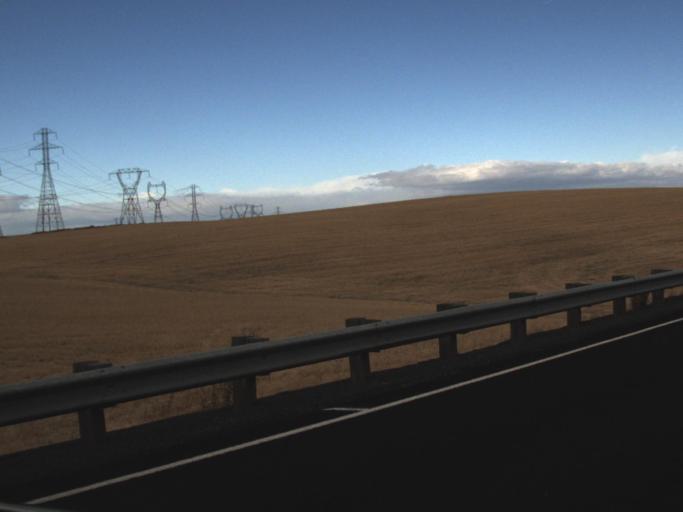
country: US
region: Washington
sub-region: Okanogan County
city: Coulee Dam
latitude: 47.8817
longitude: -118.8513
